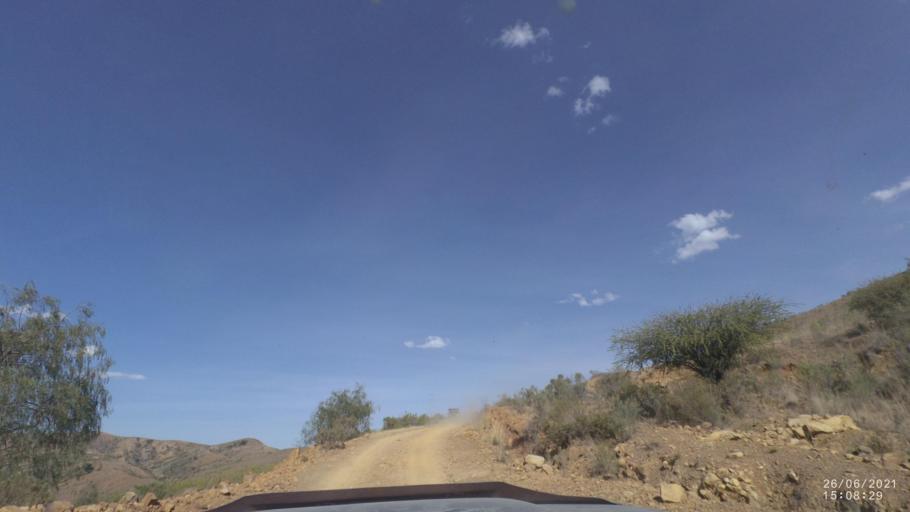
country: BO
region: Cochabamba
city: Mizque
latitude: -17.9482
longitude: -65.6403
